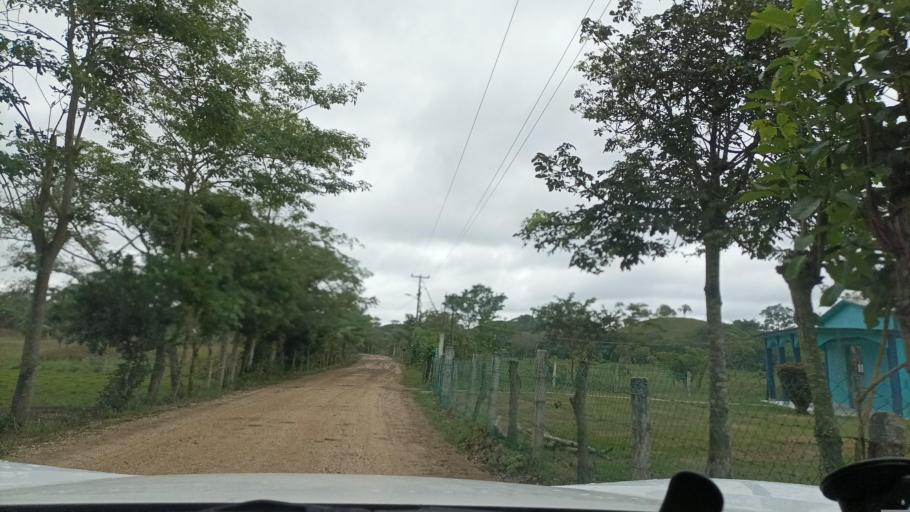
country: MX
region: Veracruz
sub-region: Moloacan
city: Cuichapa
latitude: 17.7843
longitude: -94.3882
